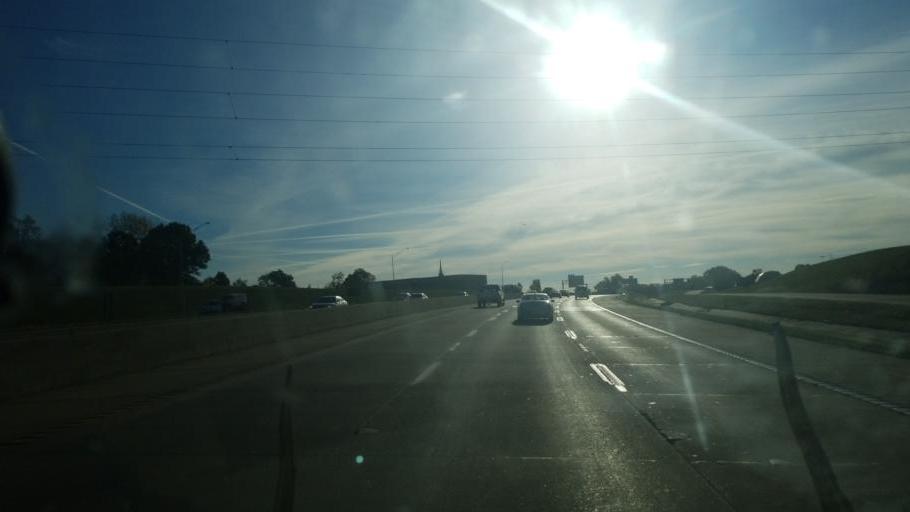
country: US
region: Missouri
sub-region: Saint Louis County
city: Normandy
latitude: 38.7197
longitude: -90.3024
